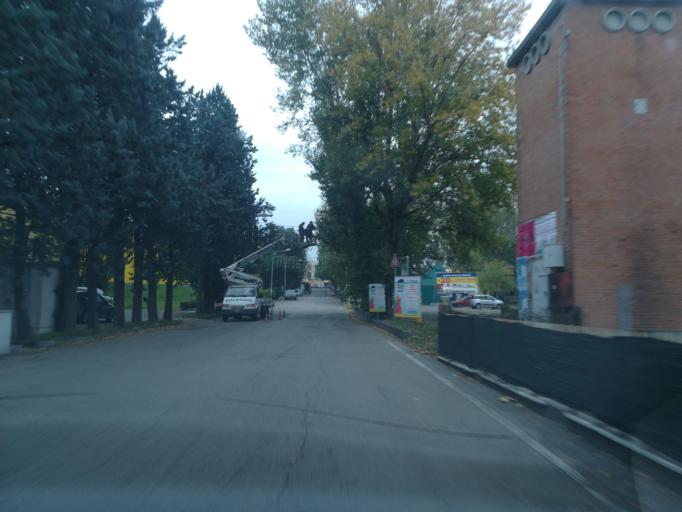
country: IT
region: Emilia-Romagna
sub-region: Provincia di Bologna
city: Toscanella
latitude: 44.3843
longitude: 11.6318
